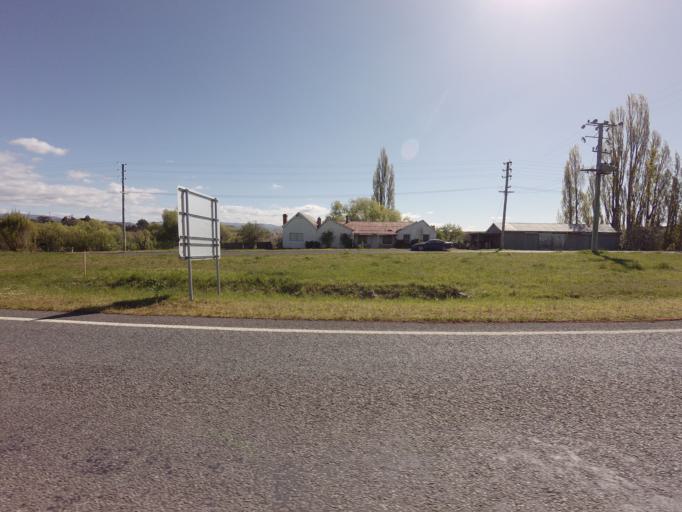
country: AU
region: Tasmania
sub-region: Derwent Valley
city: New Norfolk
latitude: -42.6889
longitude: 146.9418
